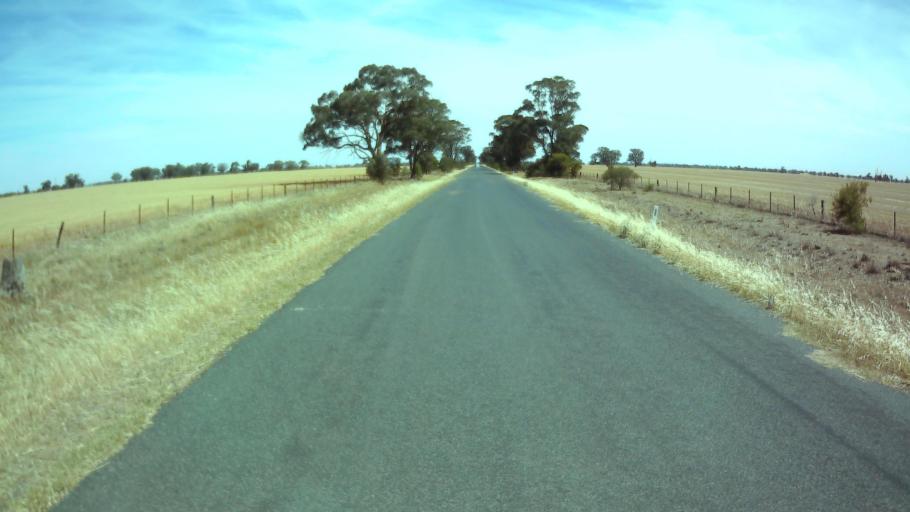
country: AU
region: New South Wales
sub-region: Weddin
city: Grenfell
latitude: -33.9620
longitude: 147.7817
